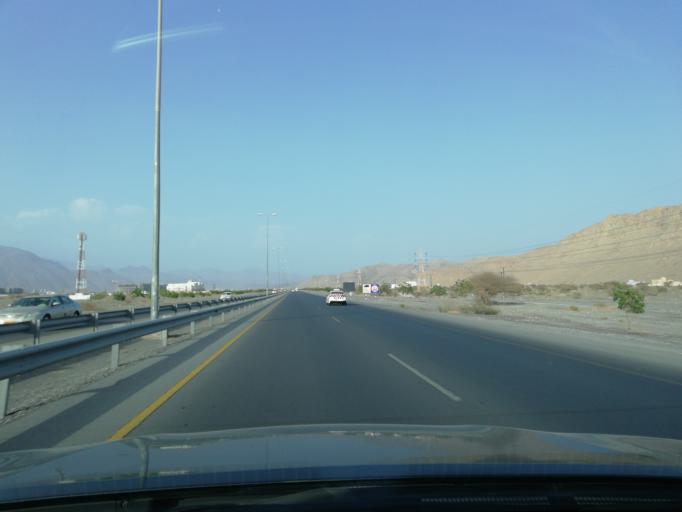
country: OM
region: Muhafazat ad Dakhiliyah
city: Nizwa
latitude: 22.8624
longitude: 57.5939
